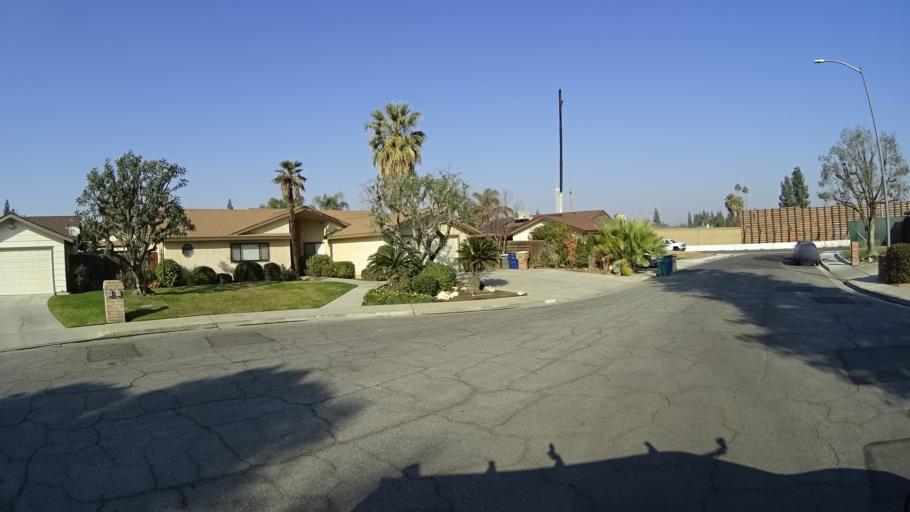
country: US
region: California
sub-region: Kern County
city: Bakersfield
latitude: 35.3635
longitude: -119.0541
